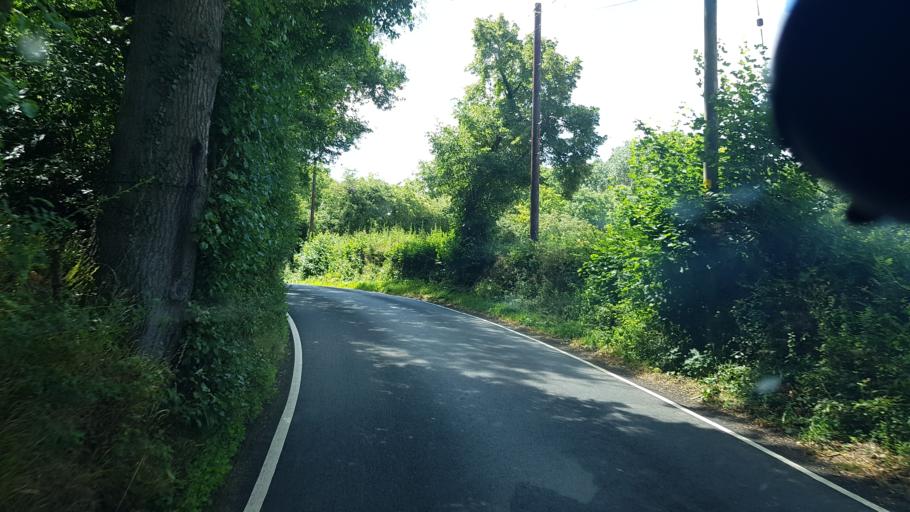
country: GB
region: England
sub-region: Kent
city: Edenbridge
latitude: 51.2130
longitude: 0.1305
